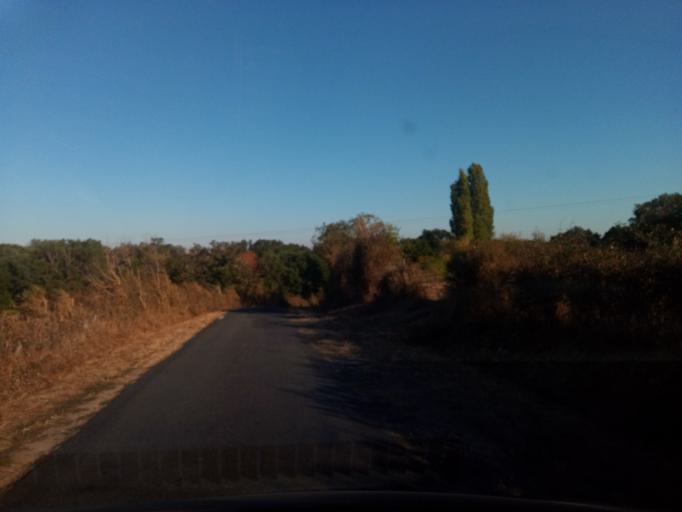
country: FR
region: Poitou-Charentes
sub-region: Departement de la Vienne
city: Montmorillon
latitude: 46.4100
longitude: 0.8686
